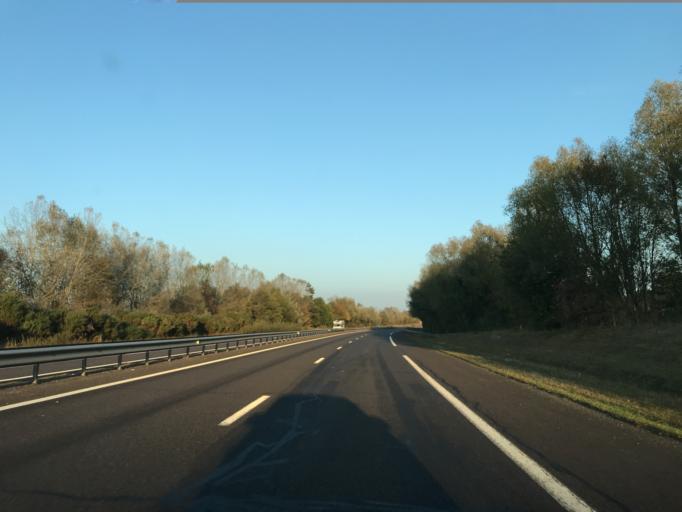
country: FR
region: Lower Normandy
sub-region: Departement de l'Orne
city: Mortagne-au-Perche
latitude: 48.5145
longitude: 0.4337
